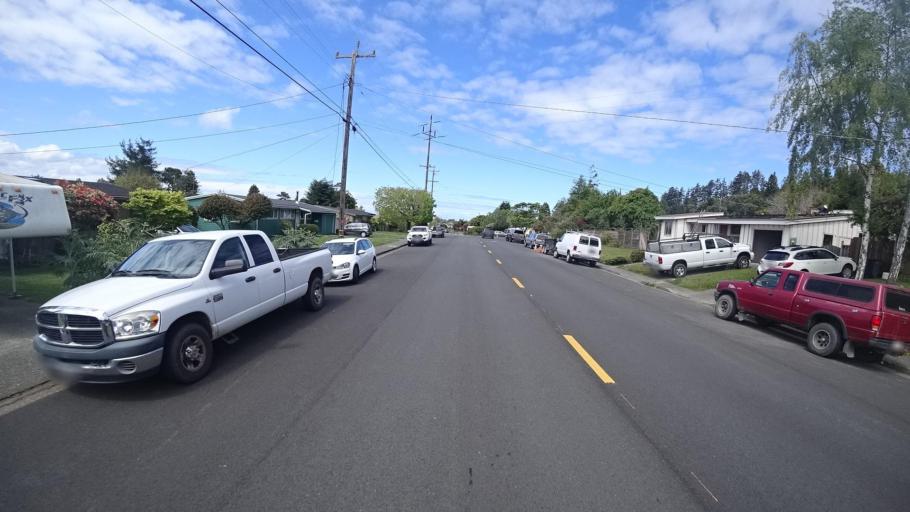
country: US
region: California
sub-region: Humboldt County
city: Bayside
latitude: 40.8585
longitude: -124.0667
